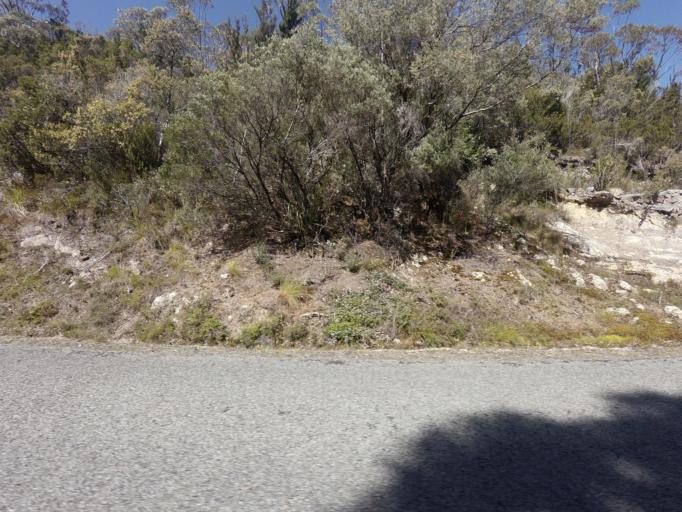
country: AU
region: Tasmania
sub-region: Huon Valley
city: Geeveston
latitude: -42.8064
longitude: 146.3939
